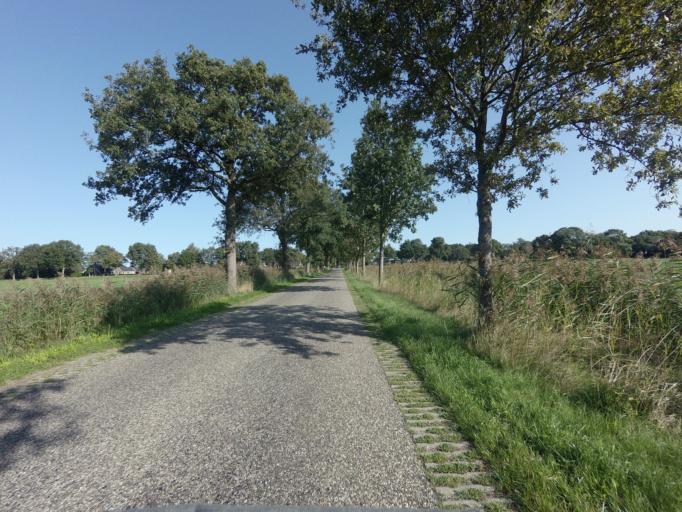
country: NL
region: Overijssel
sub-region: Gemeente Raalte
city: Raalte
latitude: 52.4372
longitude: 6.3020
